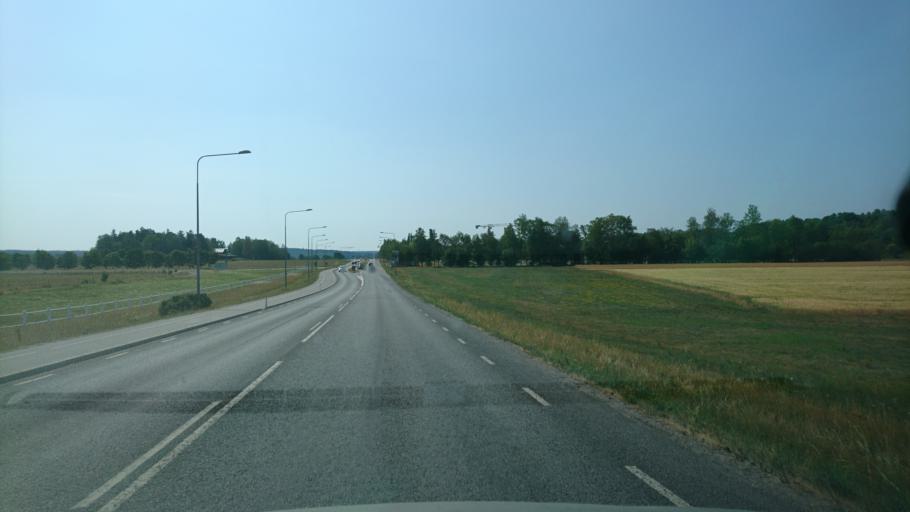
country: SE
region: Uppsala
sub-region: Uppsala Kommun
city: Uppsala
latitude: 59.8204
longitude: 17.6470
